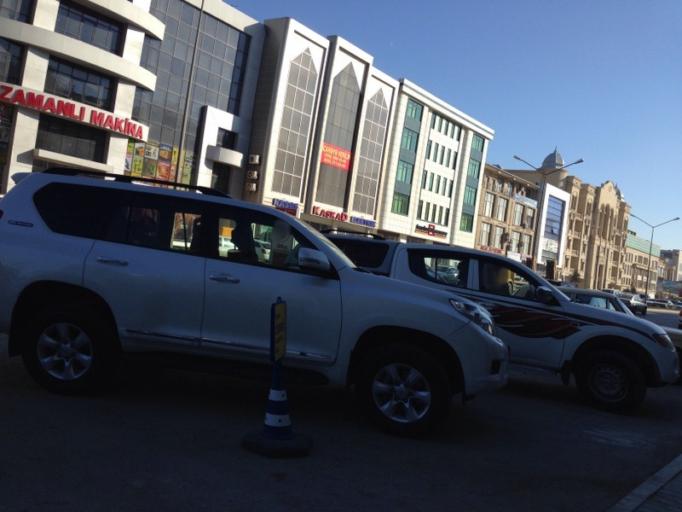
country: AZ
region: Baki
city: Baku
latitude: 40.4138
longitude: 49.8599
